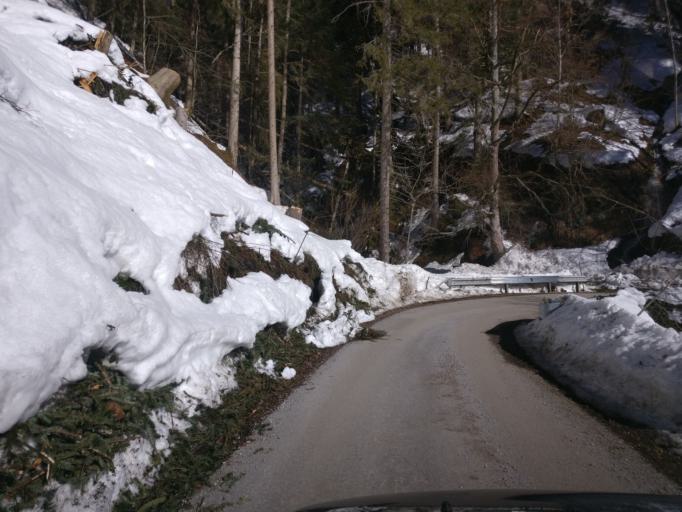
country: AT
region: Salzburg
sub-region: Politischer Bezirk Sankt Johann im Pongau
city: Wagrain
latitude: 47.3378
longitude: 13.2511
